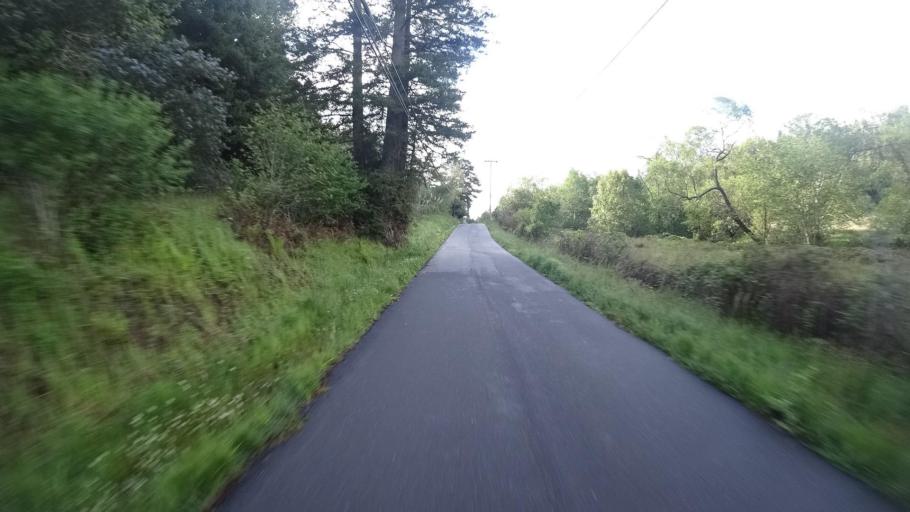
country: US
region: California
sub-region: Humboldt County
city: Arcata
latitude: 40.8884
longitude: -124.0379
